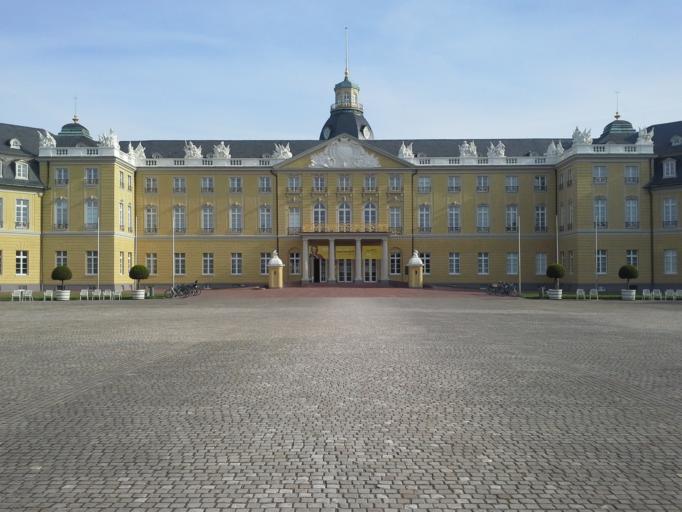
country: DE
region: Baden-Wuerttemberg
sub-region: Karlsruhe Region
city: Karlsruhe
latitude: 49.0128
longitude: 8.4043
